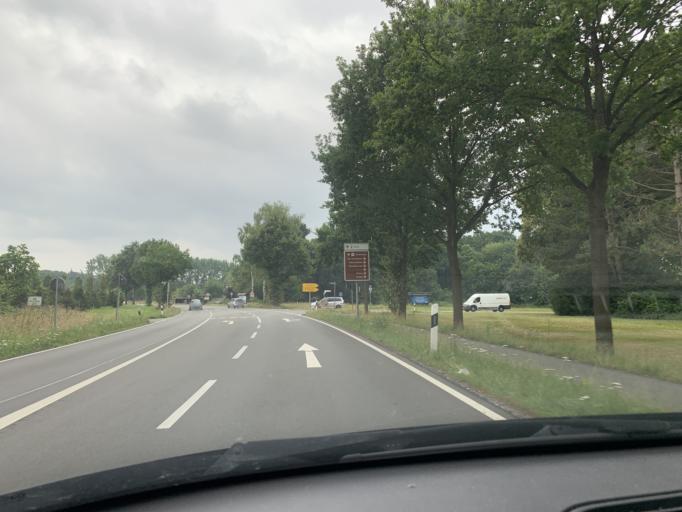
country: DE
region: Lower Saxony
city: Bad Zwischenahn
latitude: 53.2065
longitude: 8.0402
